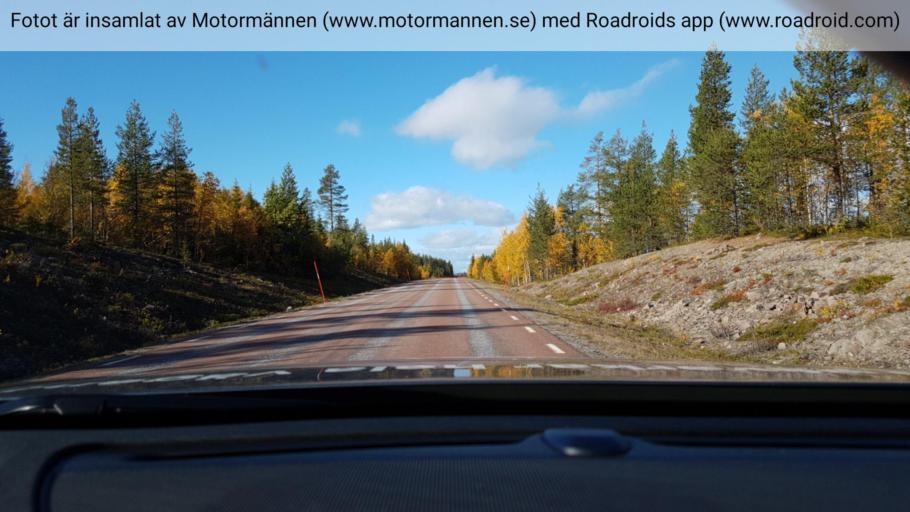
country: SE
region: Norrbotten
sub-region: Arjeplogs Kommun
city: Arjeplog
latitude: 66.0568
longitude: 17.9841
